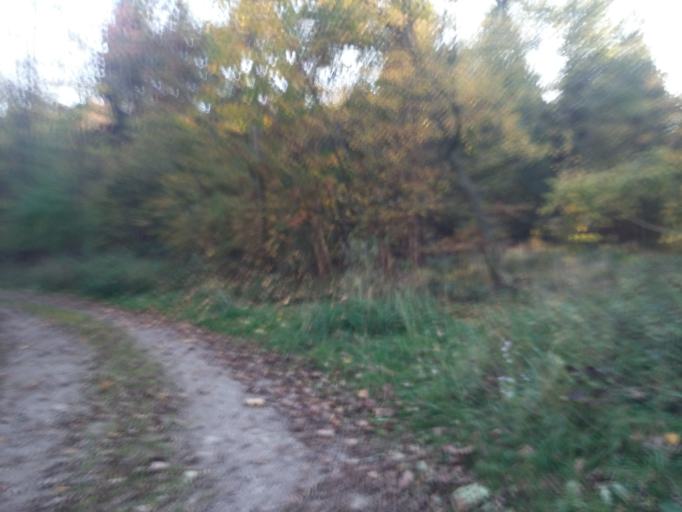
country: DE
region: Bavaria
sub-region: Upper Bavaria
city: Haar
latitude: 48.1108
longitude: 11.7442
